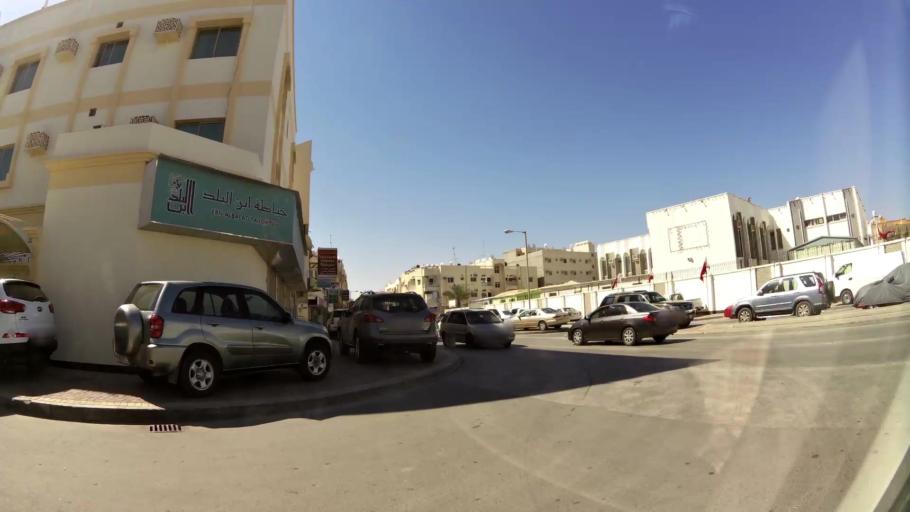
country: BH
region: Muharraq
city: Al Muharraq
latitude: 26.2544
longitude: 50.6199
